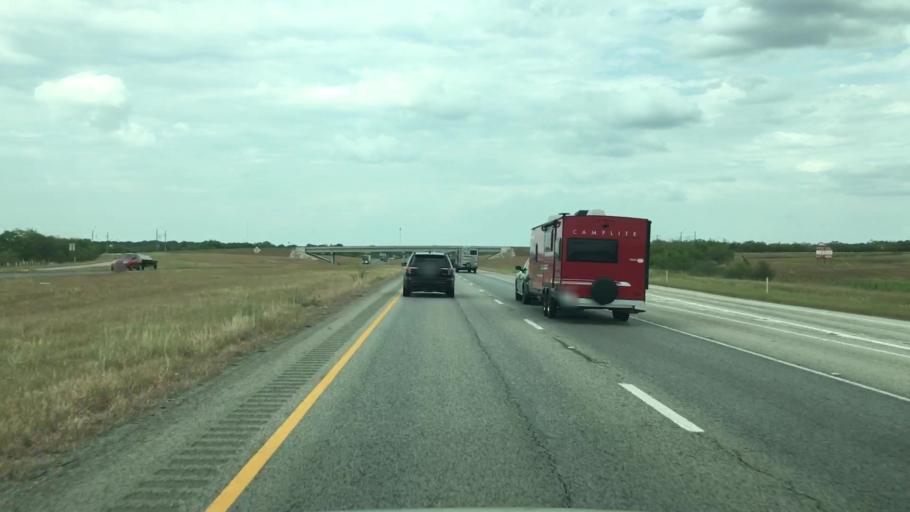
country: US
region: Texas
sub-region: Atascosa County
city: Pleasanton
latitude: 29.1027
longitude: -98.4324
